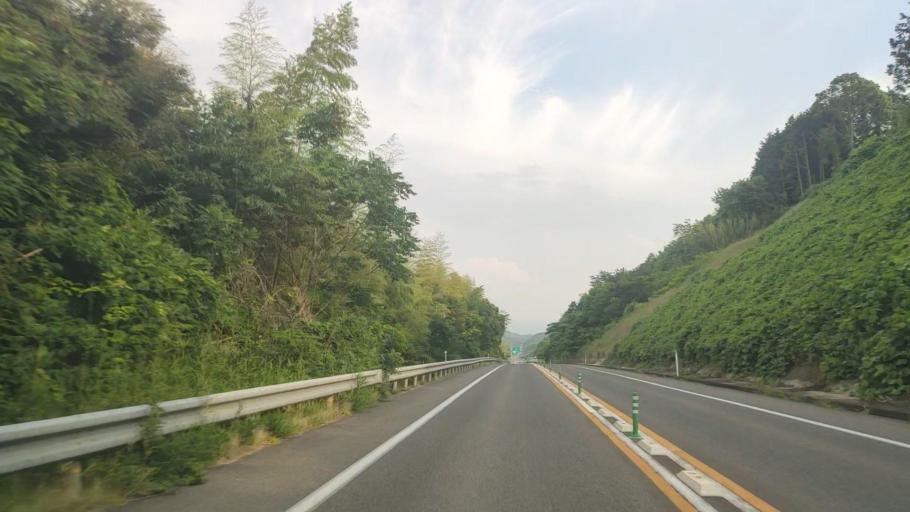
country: JP
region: Tottori
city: Kurayoshi
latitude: 35.4728
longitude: 133.8069
